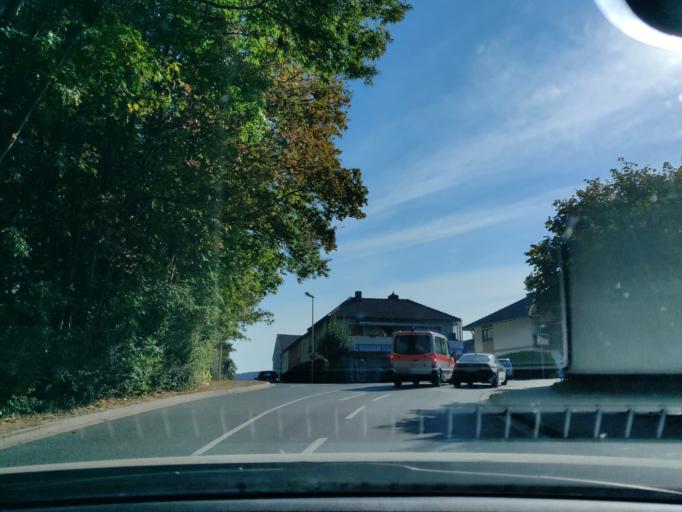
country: DE
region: Hesse
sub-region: Regierungsbezirk Kassel
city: Bad Wildungen
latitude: 51.1191
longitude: 9.1361
